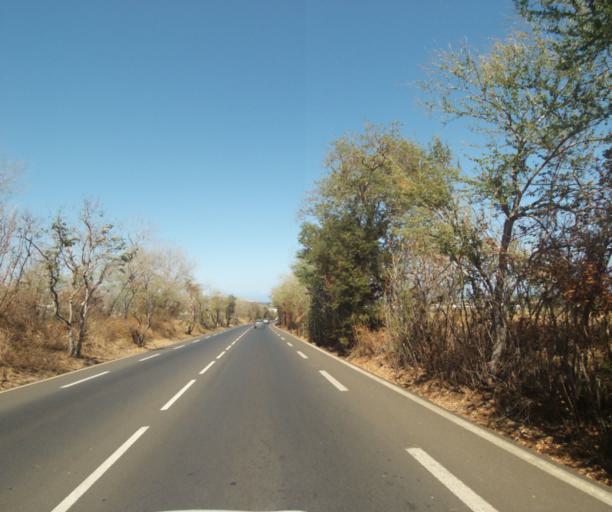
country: RE
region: Reunion
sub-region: Reunion
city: Saint-Paul
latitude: -20.9833
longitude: 55.3030
